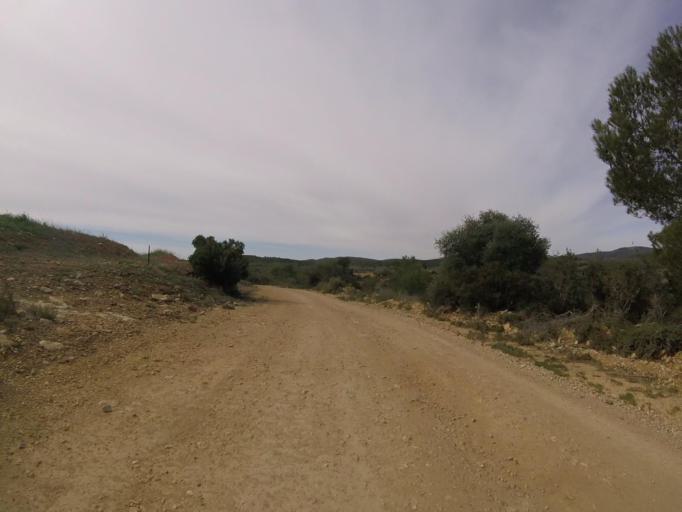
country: ES
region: Valencia
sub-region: Provincia de Castello
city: Torreblanca
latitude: 40.2003
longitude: 0.1357
